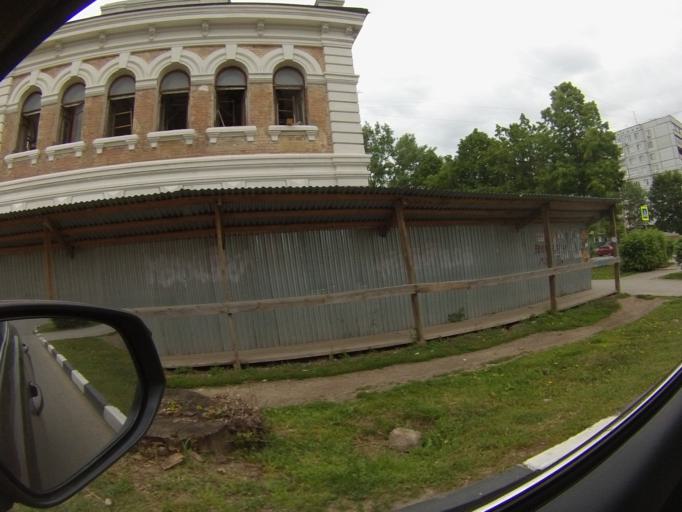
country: RU
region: Tula
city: Tula
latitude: 54.1935
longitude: 37.6013
